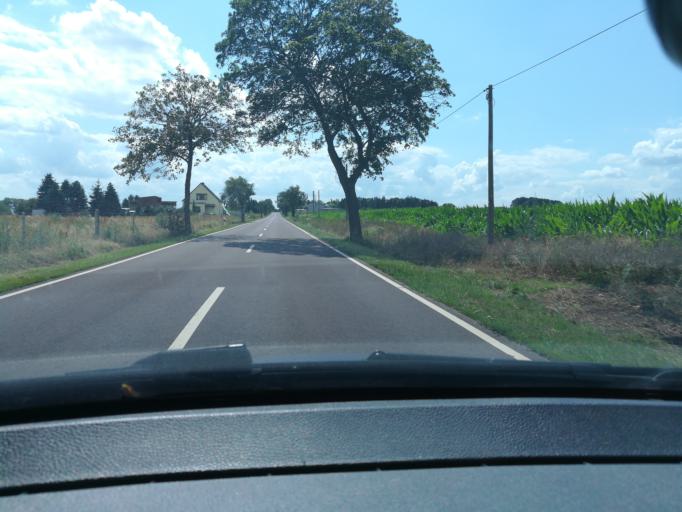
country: DE
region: Saxony-Anhalt
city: Rogatz
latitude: 52.3336
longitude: 11.7788
